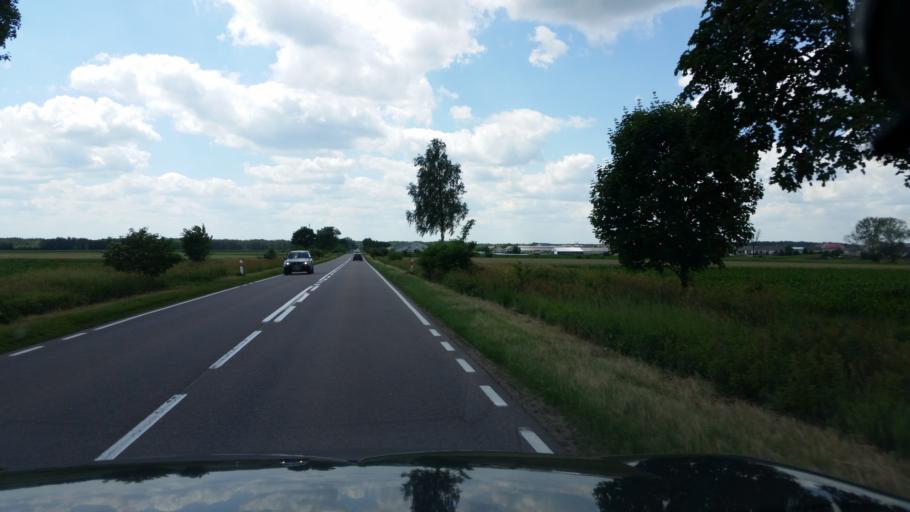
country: PL
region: Podlasie
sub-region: Powiat lomzynski
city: Sniadowo
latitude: 53.0107
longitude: 21.9444
